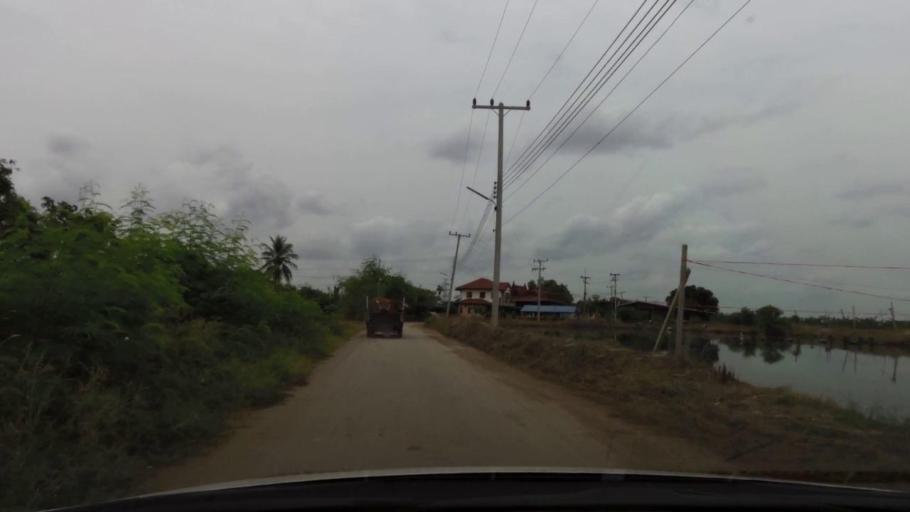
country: TH
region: Samut Sakhon
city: Ban Phaeo
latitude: 13.6215
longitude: 100.0283
